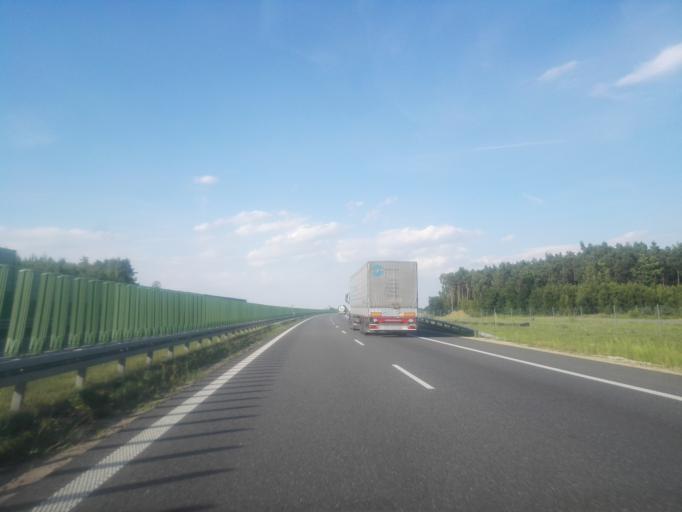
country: PL
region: Lower Silesian Voivodeship
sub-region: Powiat olesnicki
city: Miedzyborz
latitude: 51.2948
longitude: 17.5826
